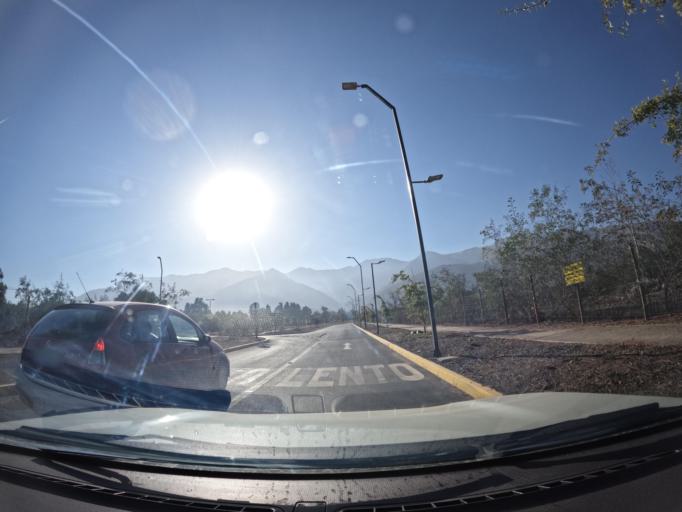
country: CL
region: Santiago Metropolitan
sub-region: Provincia de Santiago
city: Villa Presidente Frei, Nunoa, Santiago, Chile
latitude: -33.5021
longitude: -70.5379
